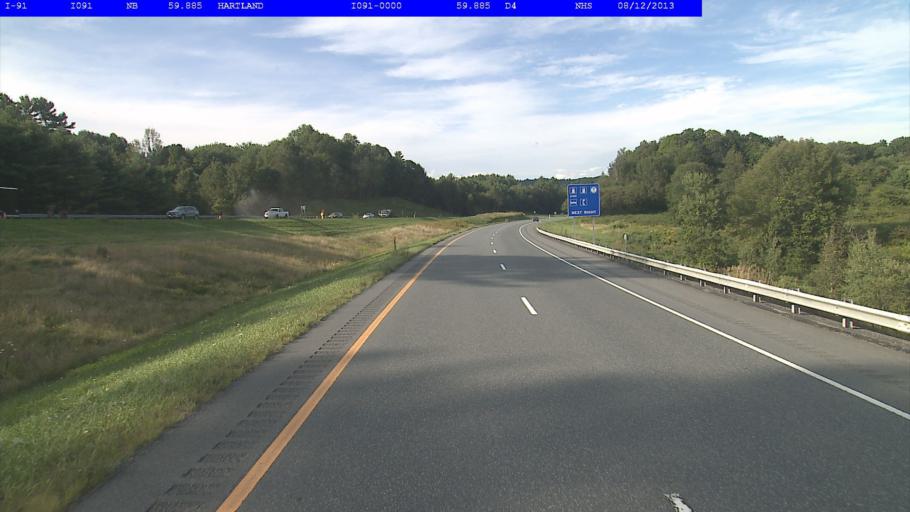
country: US
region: Vermont
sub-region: Windsor County
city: Windsor
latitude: 43.5209
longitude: -72.4084
